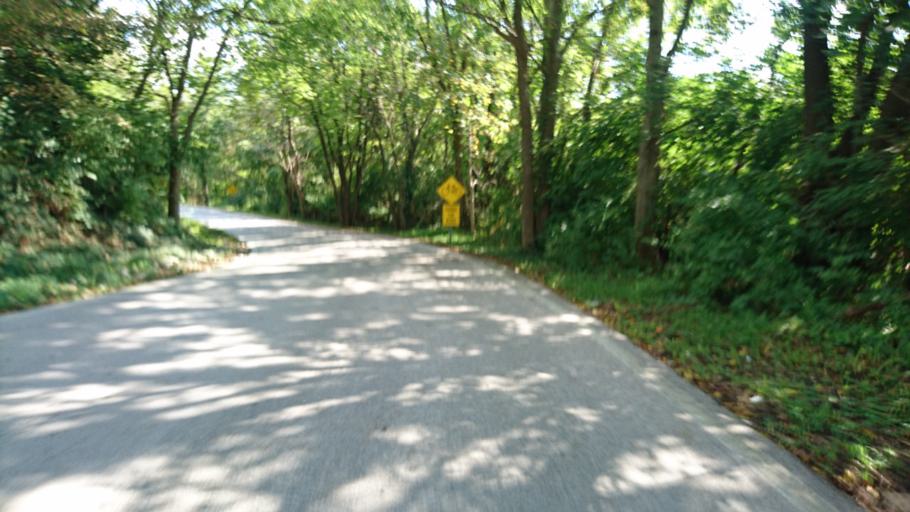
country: US
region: Missouri
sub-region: Saint Louis County
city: Wildwood
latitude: 38.5759
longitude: -90.6362
